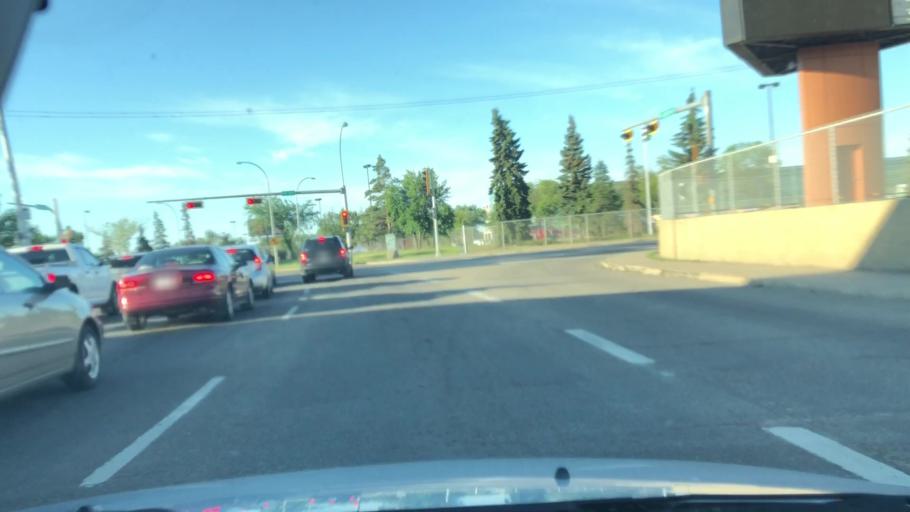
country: CA
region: Alberta
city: Edmonton
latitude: 53.5708
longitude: -113.4537
